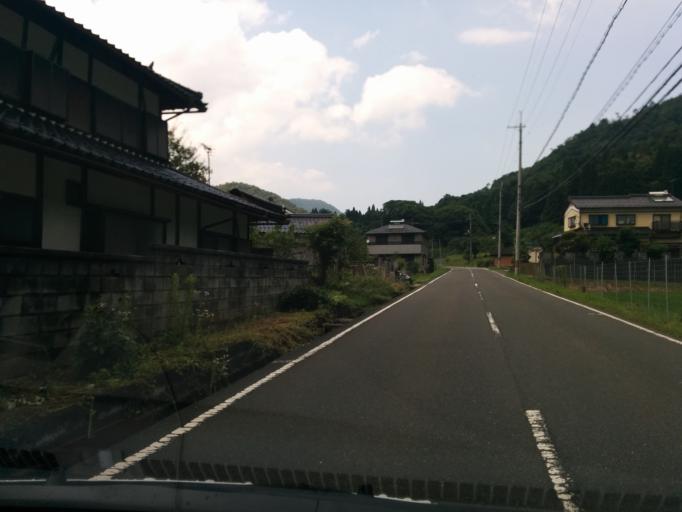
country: JP
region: Kyoto
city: Miyazu
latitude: 35.4245
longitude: 135.1571
